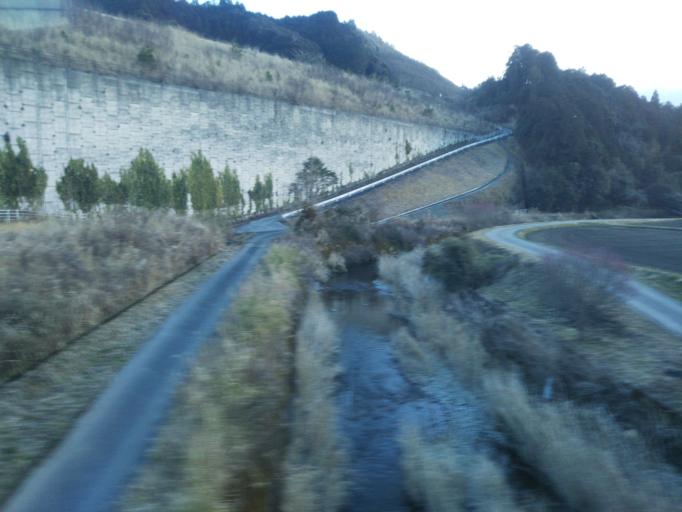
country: JP
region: Kochi
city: Susaki
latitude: 33.2769
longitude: 133.1812
